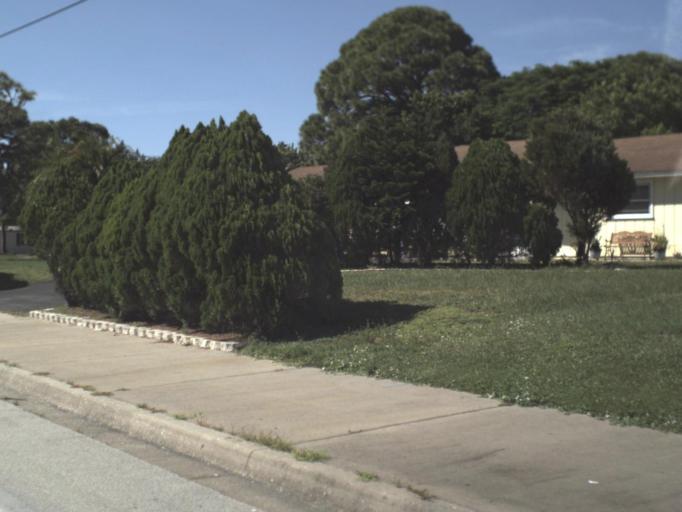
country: US
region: Florida
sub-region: Charlotte County
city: Grove City
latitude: 26.9348
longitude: -82.3255
